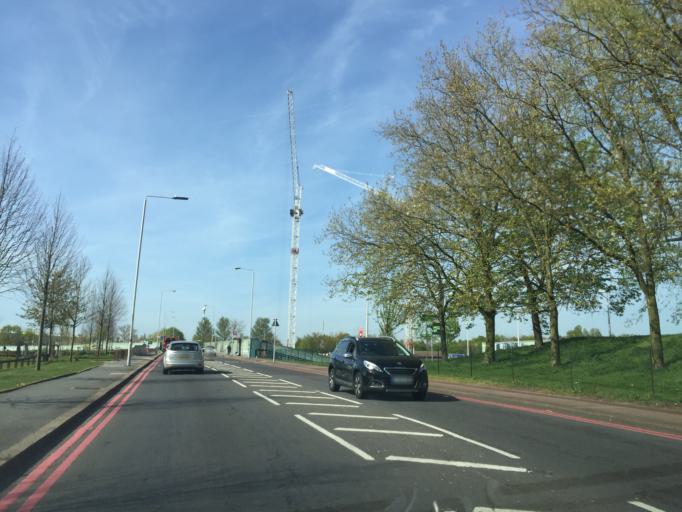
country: GB
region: England
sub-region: Greater London
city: Blackheath
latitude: 51.4600
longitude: 0.0265
